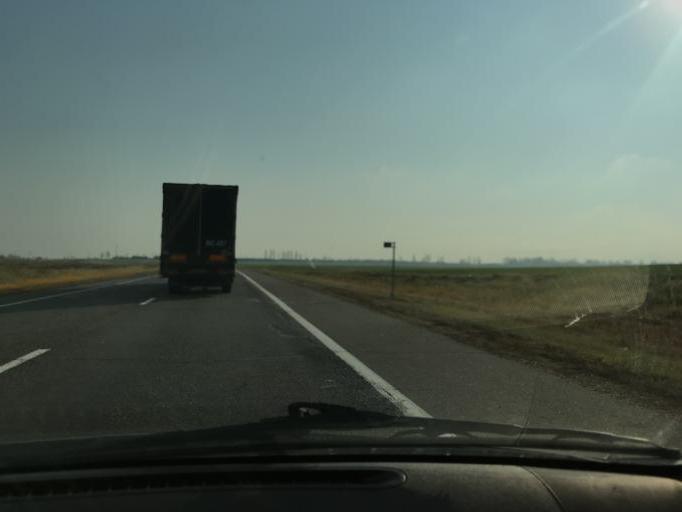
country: BY
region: Vitebsk
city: Chashniki
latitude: 55.0090
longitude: 29.1302
